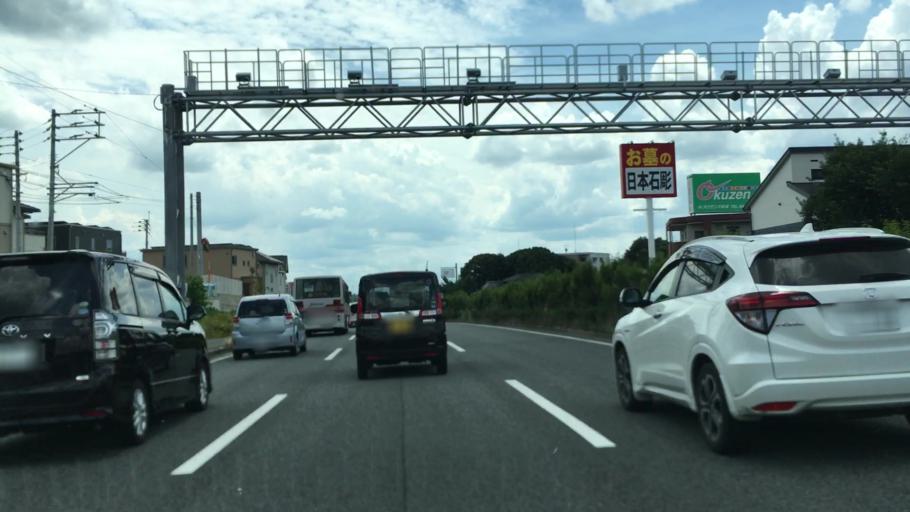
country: JP
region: Fukuoka
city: Chikushino-shi
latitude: 33.4897
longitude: 130.5355
